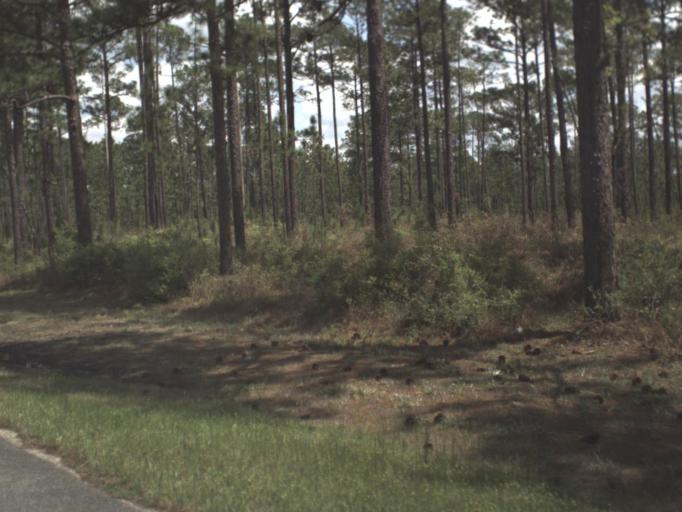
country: US
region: Florida
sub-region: Okaloosa County
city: Crestview
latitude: 30.9076
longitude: -86.6551
